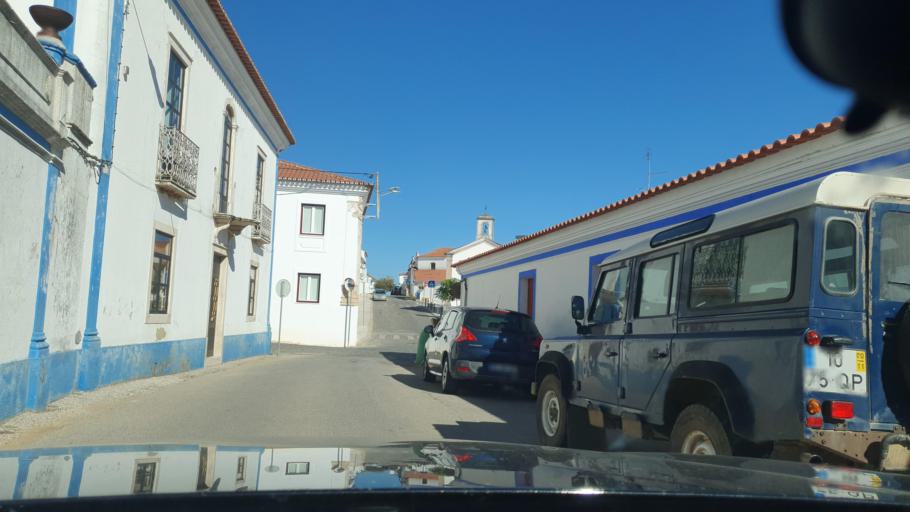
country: PT
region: Evora
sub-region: Alandroal
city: Alandroal
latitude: 38.7030
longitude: -7.4026
